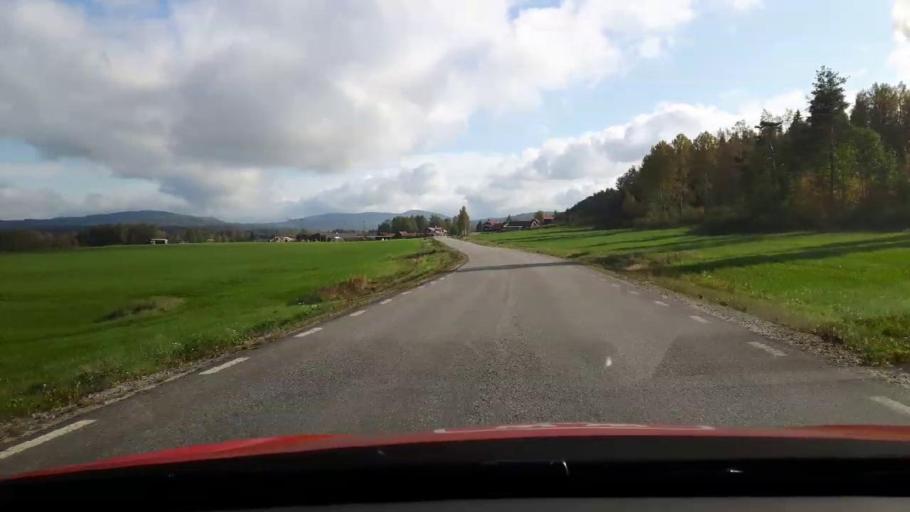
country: SE
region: Gaevleborg
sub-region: Ljusdals Kommun
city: Jaervsoe
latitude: 61.7522
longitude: 16.1426
